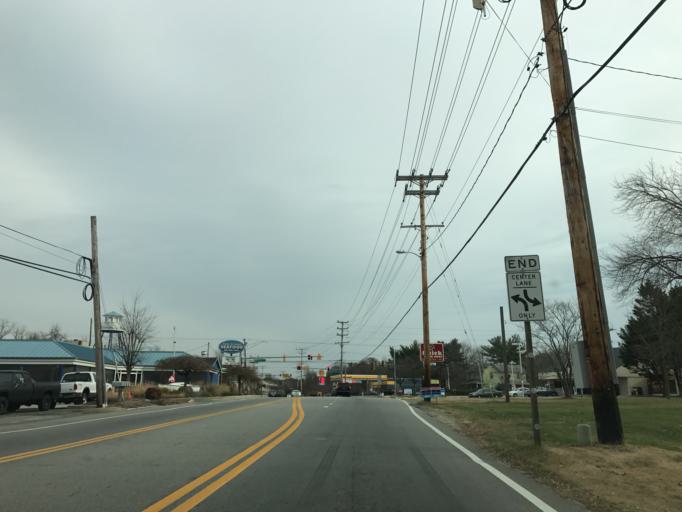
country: US
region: Maryland
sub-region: Anne Arundel County
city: Green Haven
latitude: 39.1315
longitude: -76.5644
